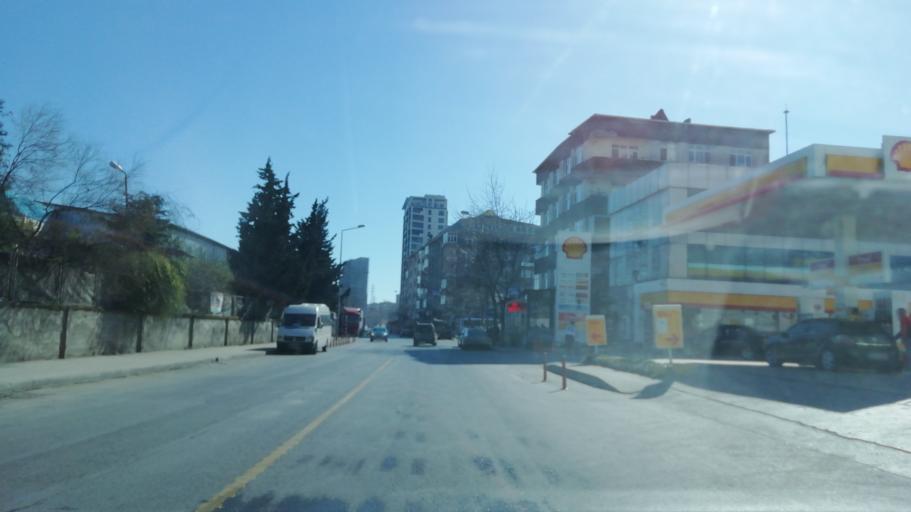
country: TR
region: Istanbul
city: Mahmutbey
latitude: 41.0248
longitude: 28.8066
